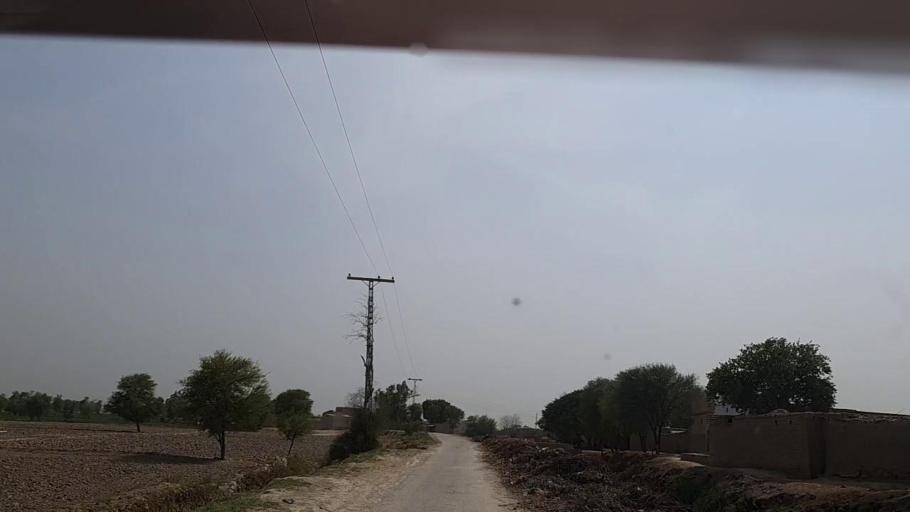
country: PK
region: Sindh
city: Khairpur Nathan Shah
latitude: 27.0629
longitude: 67.6871
